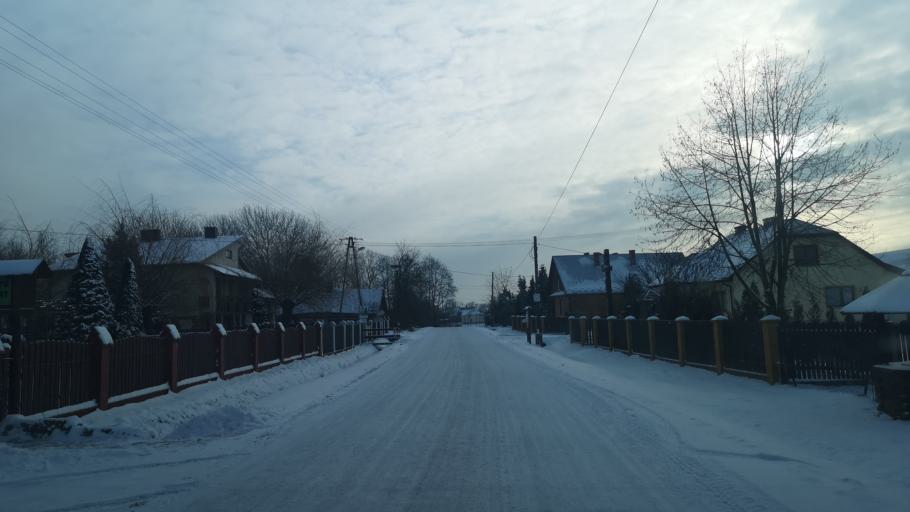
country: PL
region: Subcarpathian Voivodeship
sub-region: Powiat przeworski
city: Adamowka
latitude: 50.2606
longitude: 22.6873
